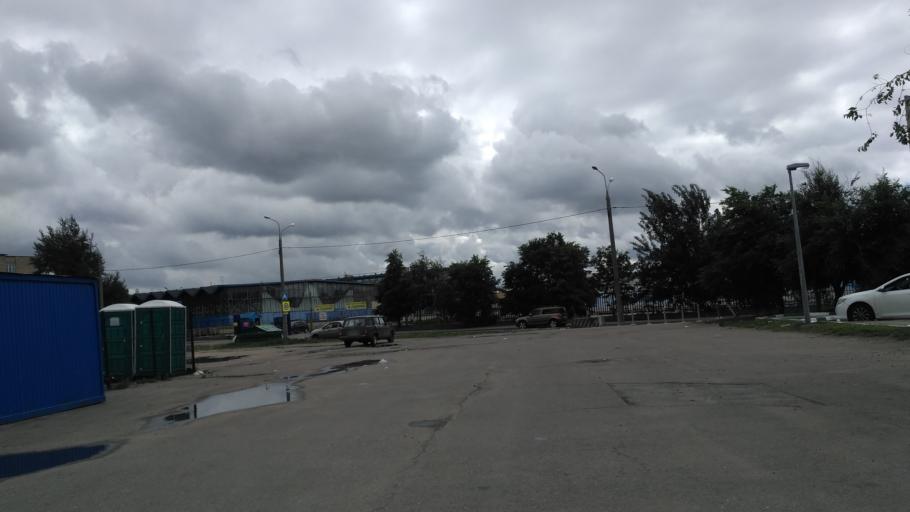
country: RU
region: Moscow
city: Metrogorodok
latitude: 55.8028
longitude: 37.7564
